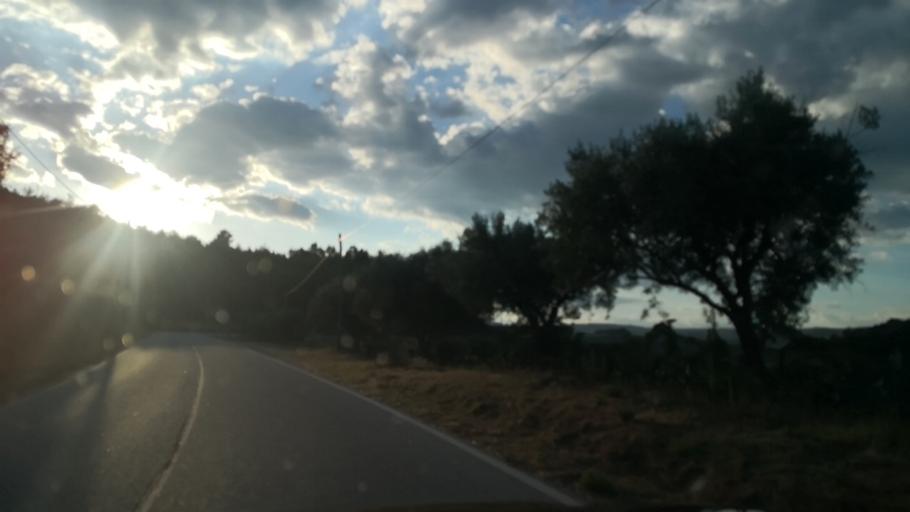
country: PT
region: Viseu
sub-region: Sao Joao da Pesqueira
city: Sao Joao da Pesqueira
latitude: 41.2605
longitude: -7.4428
